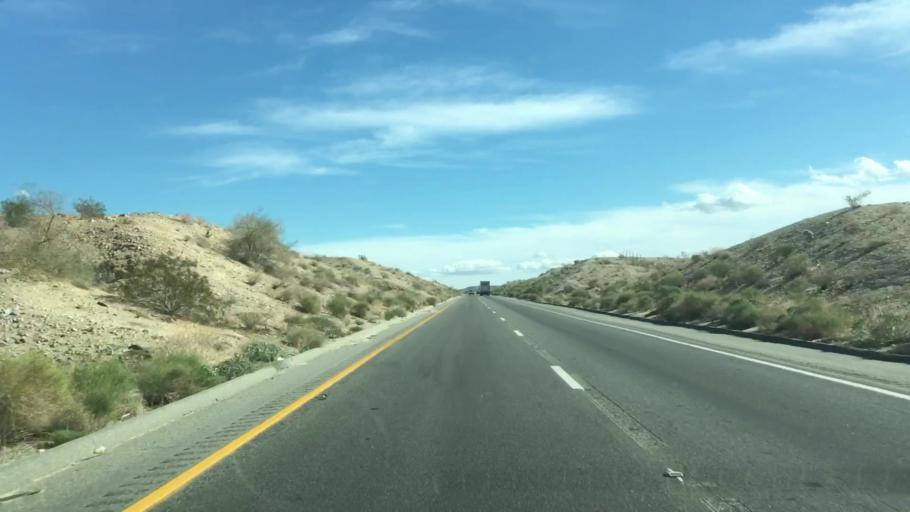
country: US
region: California
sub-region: Riverside County
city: Mecca
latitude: 33.6844
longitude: -116.0200
